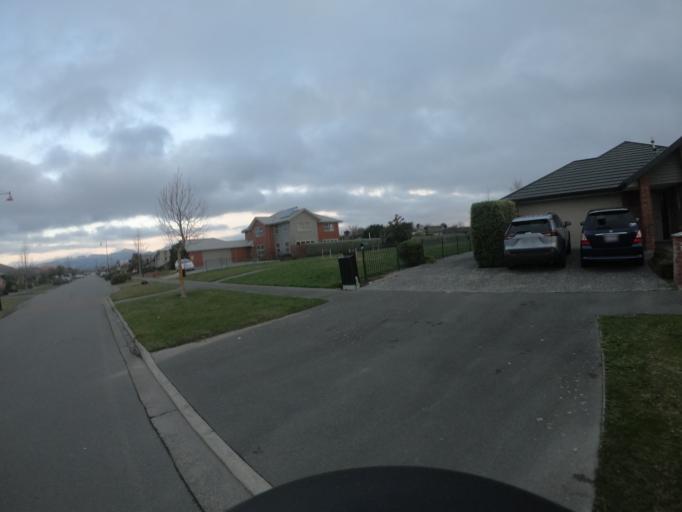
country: NZ
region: Canterbury
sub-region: Selwyn District
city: Prebbleton
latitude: -43.5651
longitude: 172.5608
